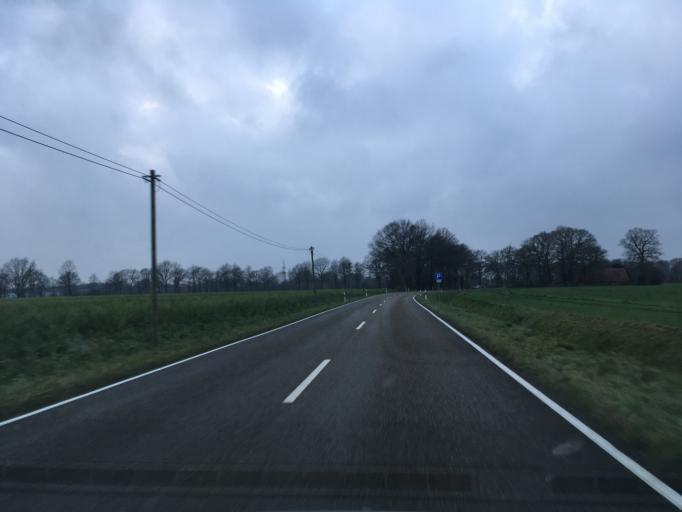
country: DE
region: North Rhine-Westphalia
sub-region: Regierungsbezirk Munster
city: Heek
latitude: 52.1757
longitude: 7.0789
